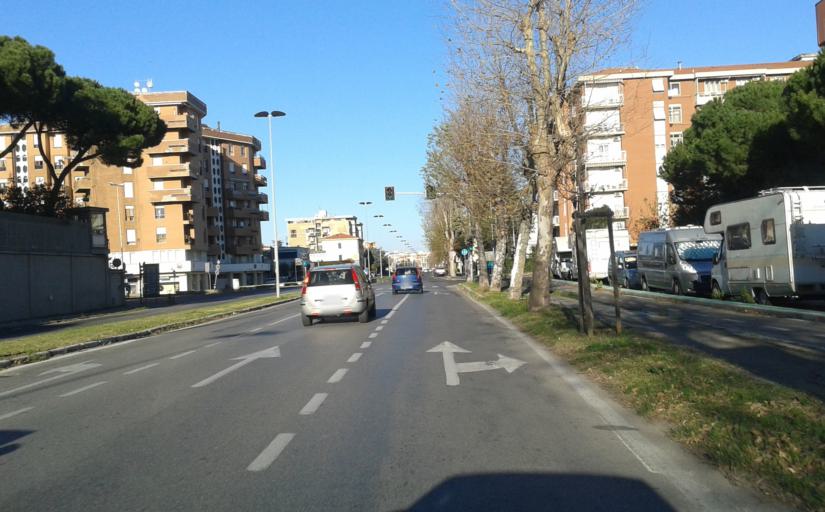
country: IT
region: Tuscany
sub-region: Provincia di Livorno
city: Livorno
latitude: 43.5402
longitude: 10.3241
